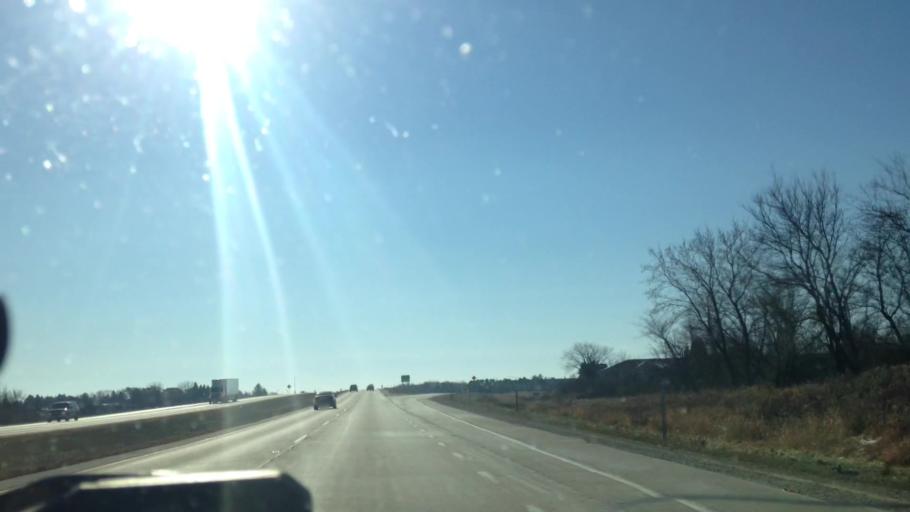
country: US
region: Wisconsin
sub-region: Washington County
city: Jackson
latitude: 43.3290
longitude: -88.1883
